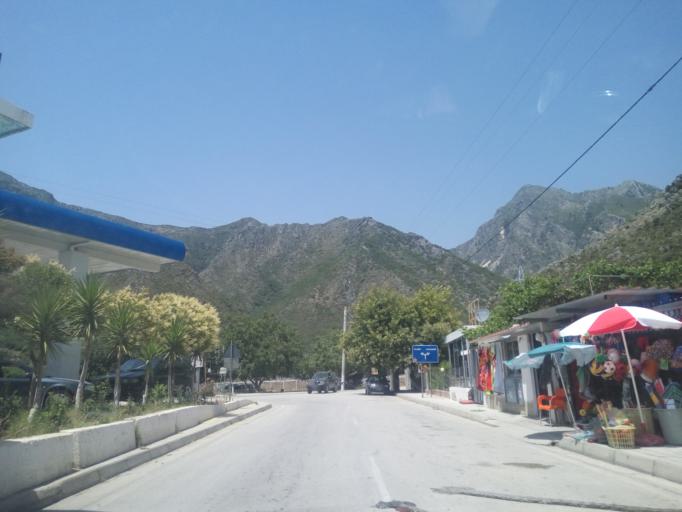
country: AL
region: Vlore
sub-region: Rrethi i Sarandes
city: Lukove
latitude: 40.0634
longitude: 19.8502
